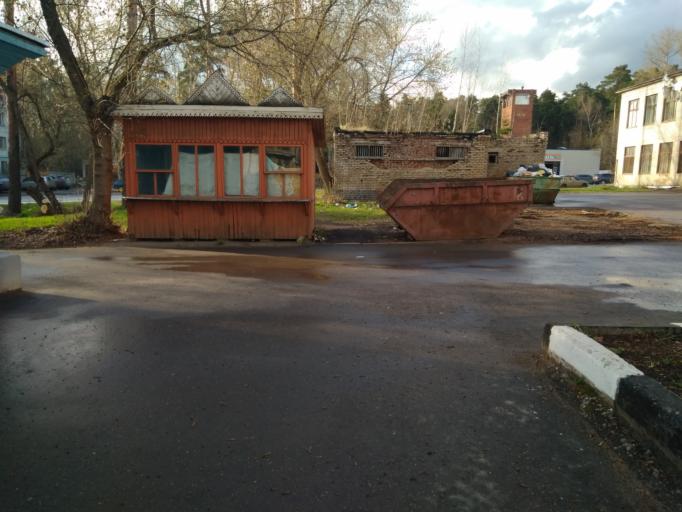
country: RU
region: Moskovskaya
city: Zhukovskiy
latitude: 55.5746
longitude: 38.1214
